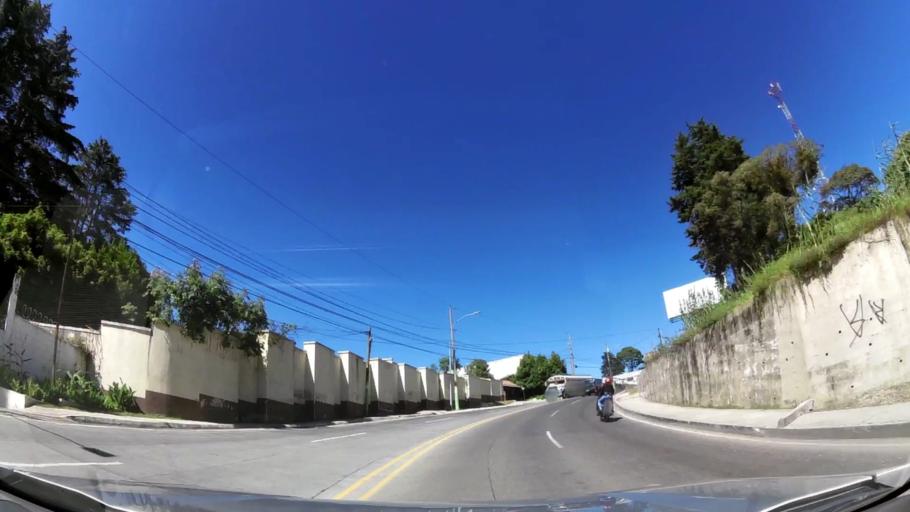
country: GT
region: Guatemala
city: San Jose Pinula
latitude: 14.5441
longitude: -90.4224
